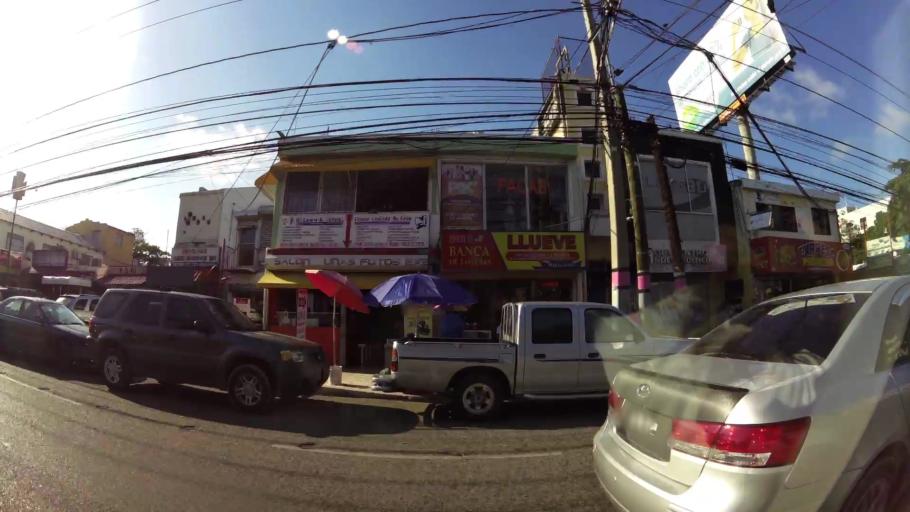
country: DO
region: Nacional
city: La Julia
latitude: 18.4503
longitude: -69.9291
